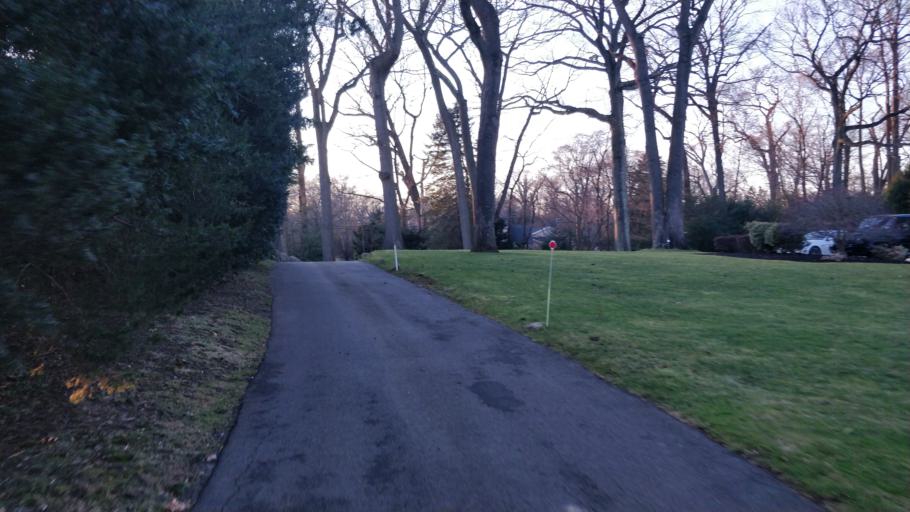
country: US
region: New York
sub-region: Nassau County
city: Locust Valley
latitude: 40.8708
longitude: -73.6125
